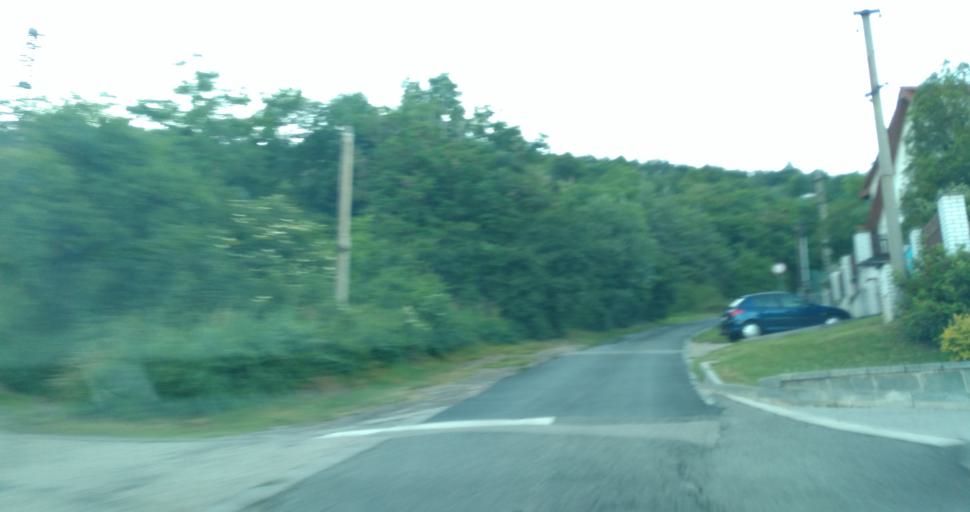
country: CZ
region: Central Bohemia
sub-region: Okres Beroun
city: Beroun
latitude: 49.9690
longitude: 14.0597
